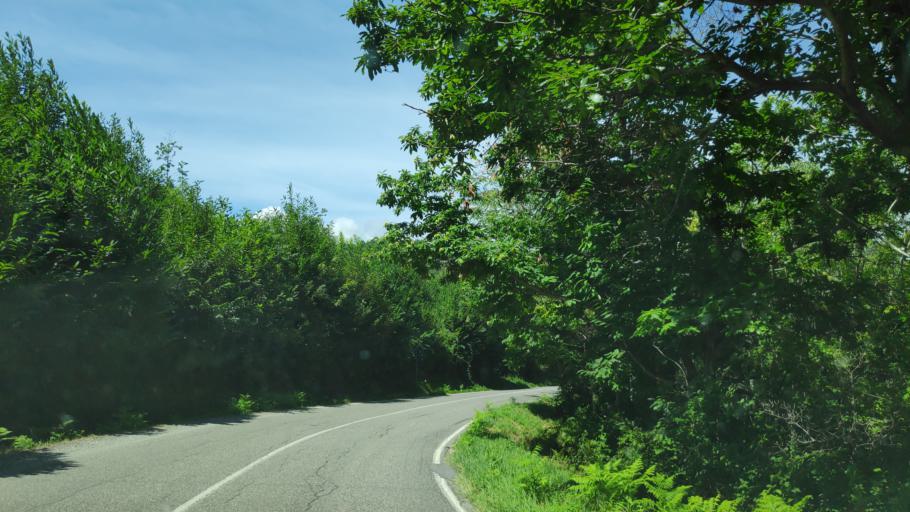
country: IT
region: Calabria
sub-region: Provincia di Catanzaro
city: Palermiti
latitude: 38.7433
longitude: 16.4520
